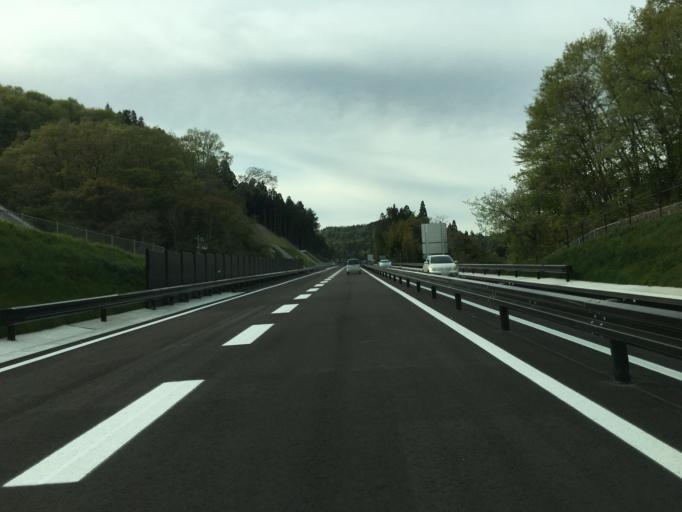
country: JP
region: Fukushima
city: Hobaramachi
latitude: 37.7716
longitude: 140.5859
